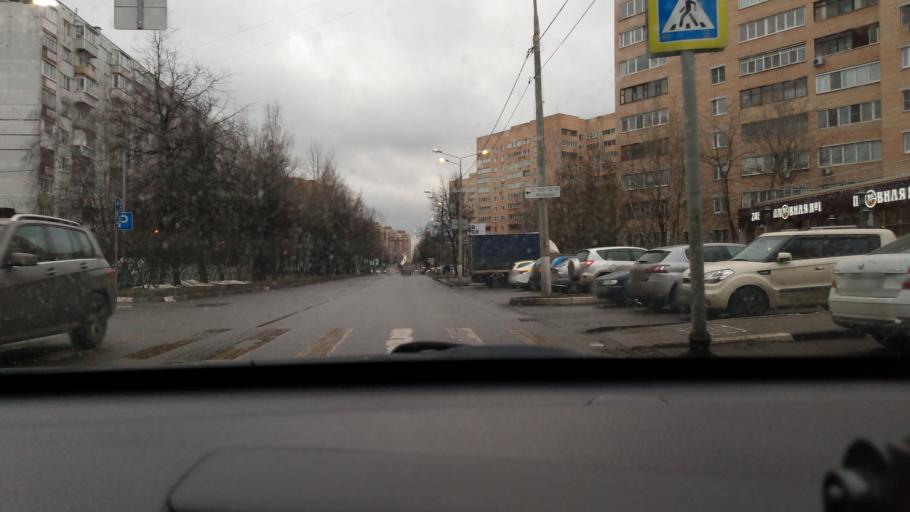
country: RU
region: Moskovskaya
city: Mytishchi
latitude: 55.9069
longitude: 37.7187
